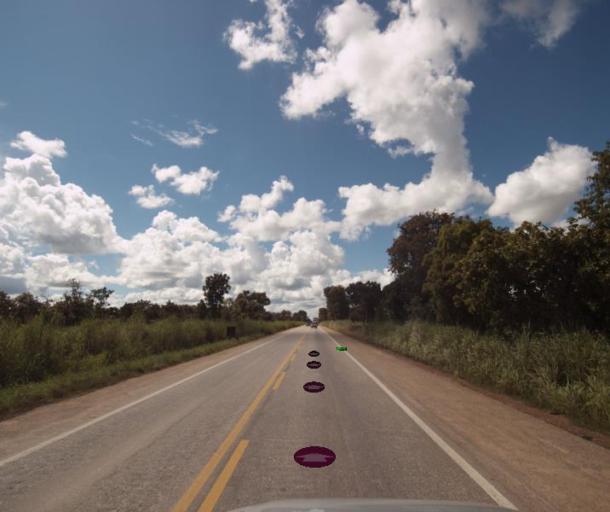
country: BR
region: Goias
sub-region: Porangatu
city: Porangatu
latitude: -13.5920
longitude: -49.0417
